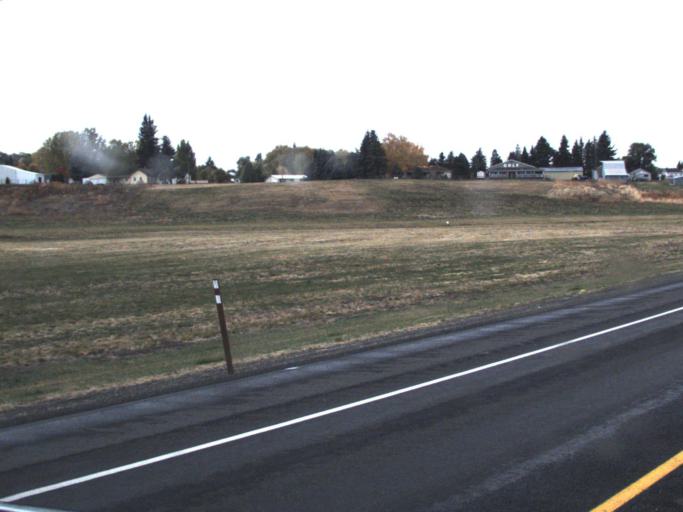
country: US
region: Washington
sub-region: Asotin County
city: Clarkston
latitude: 46.5671
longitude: -117.1181
